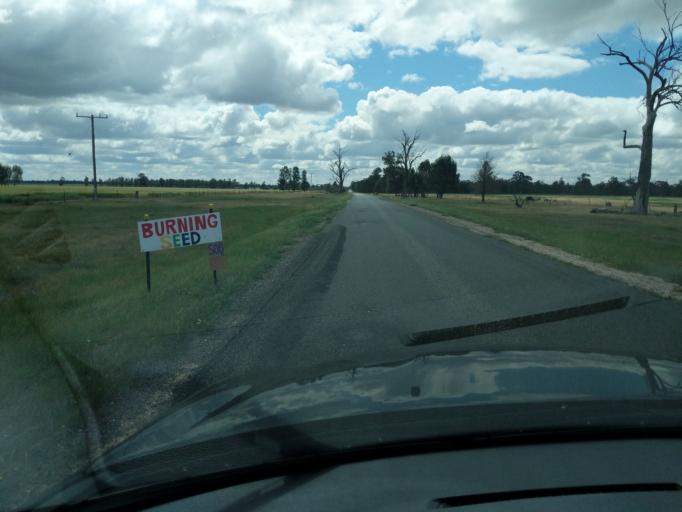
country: AU
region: New South Wales
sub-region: Coolamon
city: Coolamon
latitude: -34.8585
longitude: 146.8983
